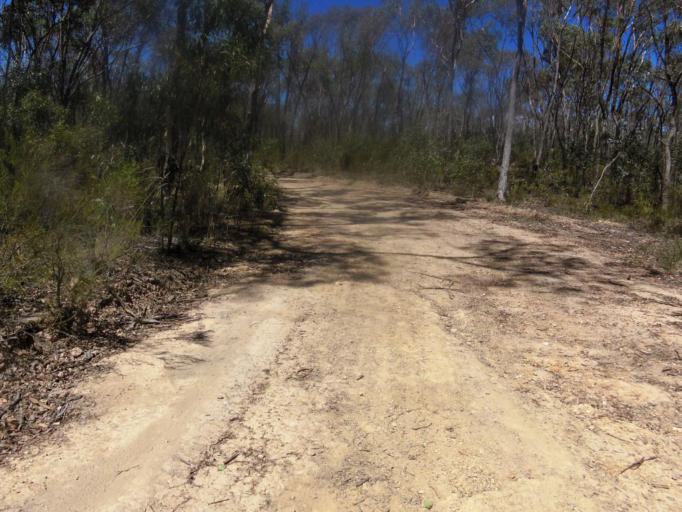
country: AU
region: Victoria
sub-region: Mount Alexander
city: Castlemaine
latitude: -37.0098
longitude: 144.1250
